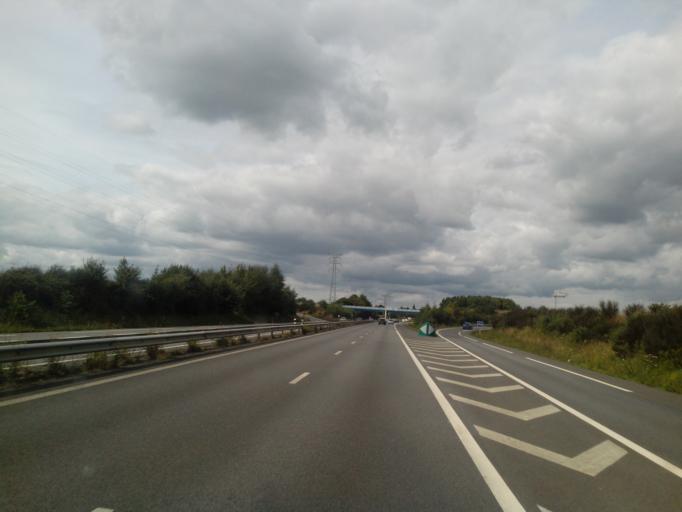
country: FR
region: Brittany
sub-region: Departement d'Ille-et-Vilaine
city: Montgermont
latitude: 48.1719
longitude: -1.7149
